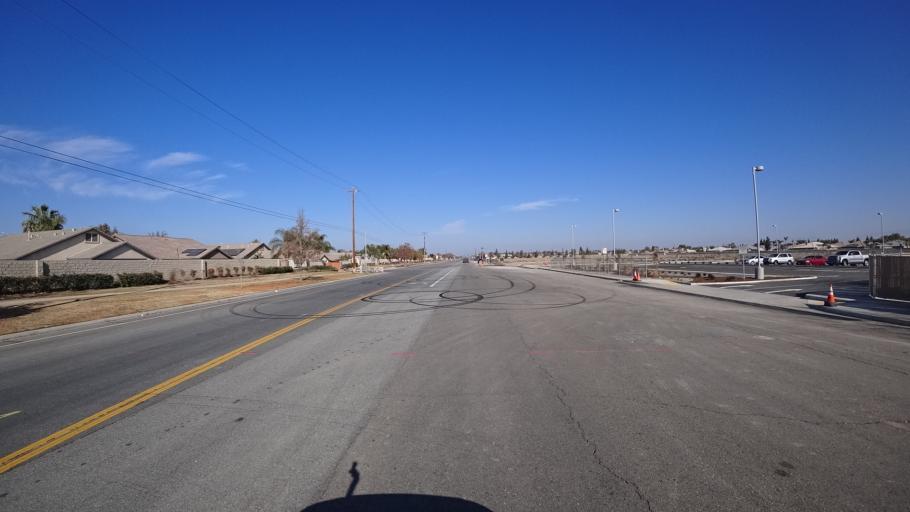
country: US
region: California
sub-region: Kern County
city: Greenfield
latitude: 35.2698
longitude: -119.0567
